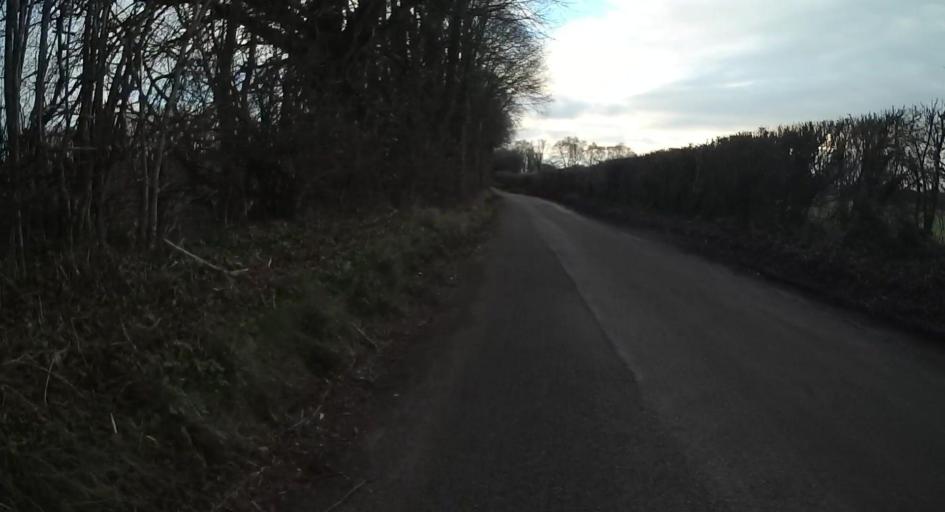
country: GB
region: England
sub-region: Hampshire
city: Swanmore
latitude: 51.0391
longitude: -1.1616
